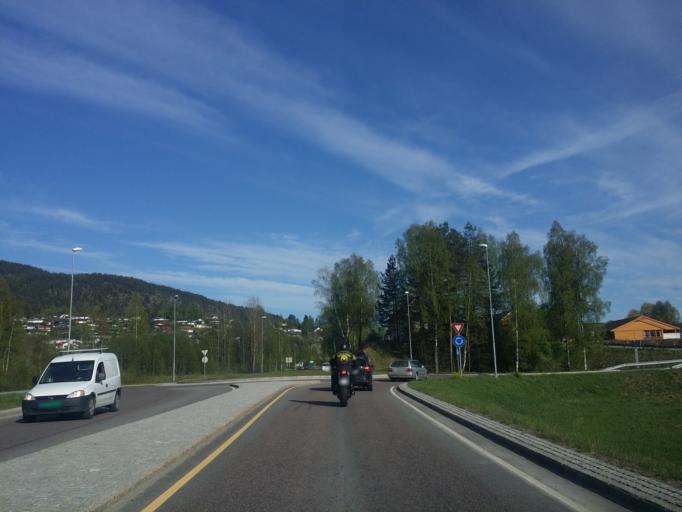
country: NO
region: Telemark
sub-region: Notodden
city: Notodden
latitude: 59.5765
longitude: 9.1893
